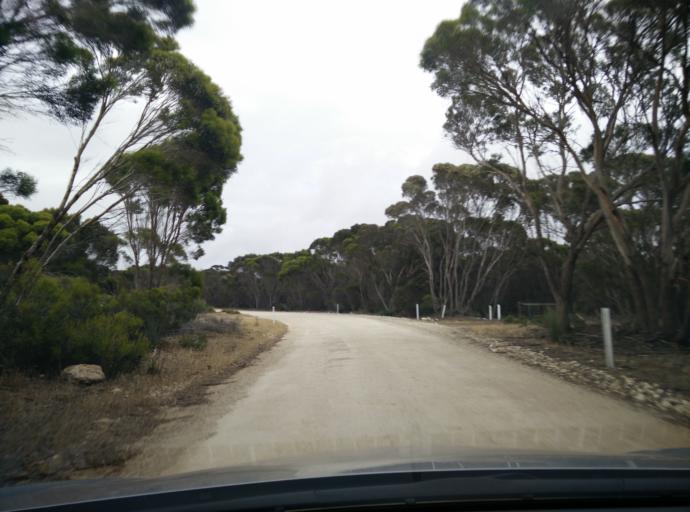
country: AU
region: South Australia
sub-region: Kangaroo Island
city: Kingscote
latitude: -35.8700
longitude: 137.5143
